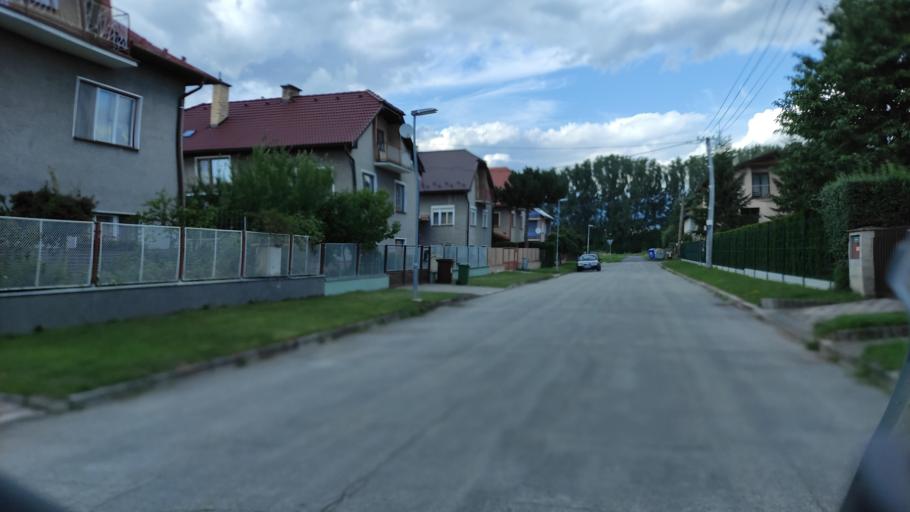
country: SK
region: Zilinsky
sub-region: Okres Liptovsky Mikulas
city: Liptovsky Mikulas
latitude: 49.0872
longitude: 19.5895
